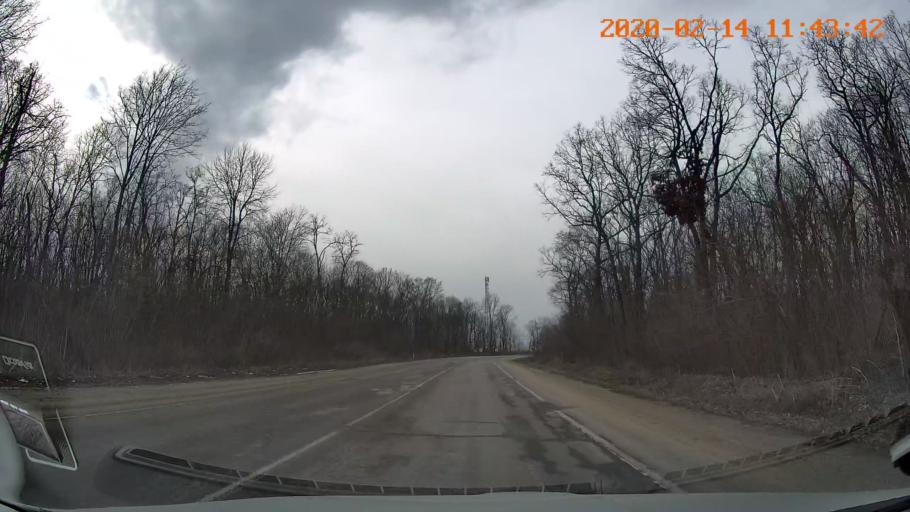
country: MD
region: Briceni
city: Briceni
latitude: 48.3316
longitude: 27.0484
